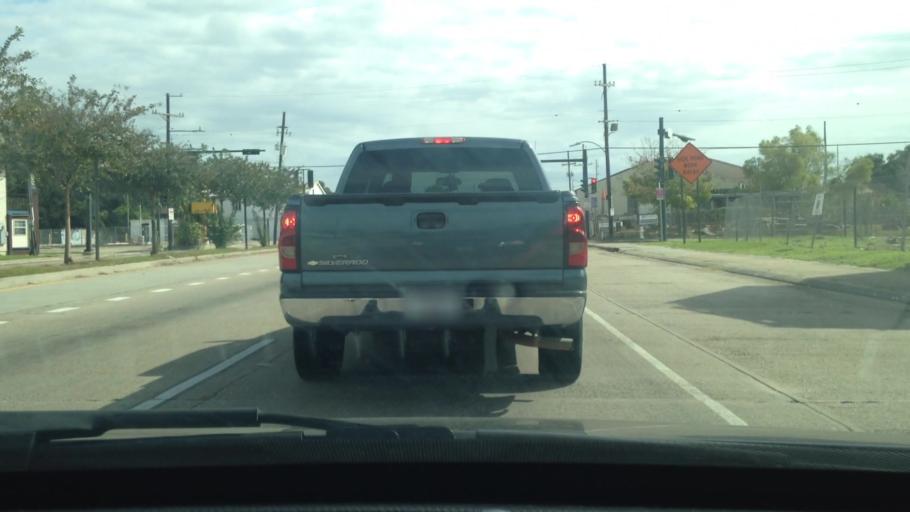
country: US
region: Louisiana
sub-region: Jefferson Parish
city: Jefferson
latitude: 29.9645
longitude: -90.1217
